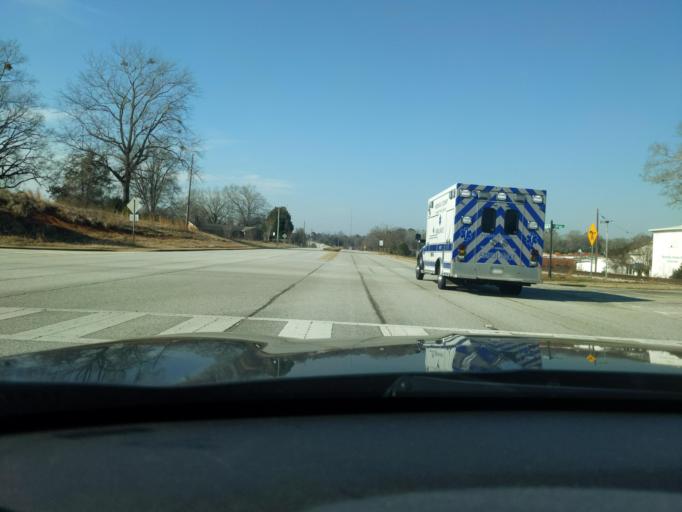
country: US
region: South Carolina
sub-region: Abbeville County
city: Calhoun Falls
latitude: 34.0949
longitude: -82.5898
